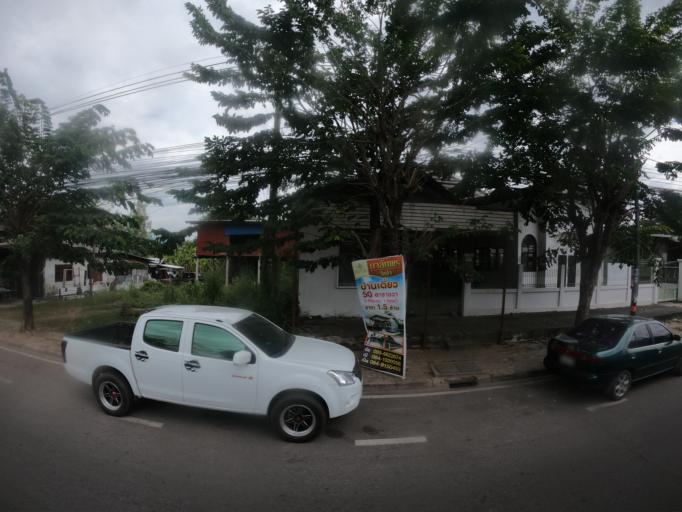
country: TH
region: Maha Sarakham
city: Maha Sarakham
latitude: 16.1952
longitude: 103.2938
